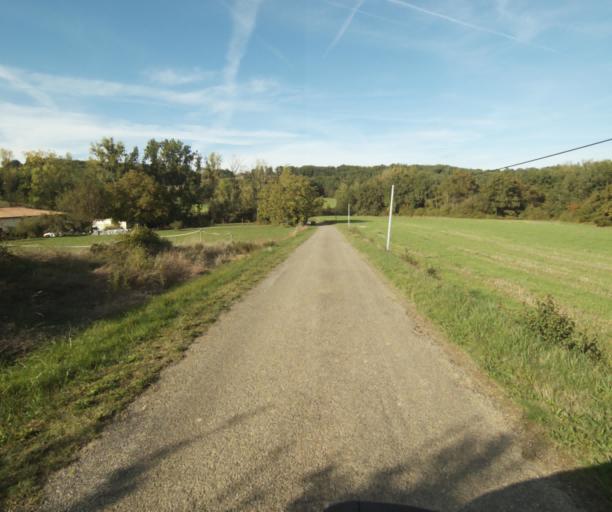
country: FR
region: Midi-Pyrenees
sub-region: Departement du Tarn-et-Garonne
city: Saint-Porquier
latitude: 43.9352
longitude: 1.1461
